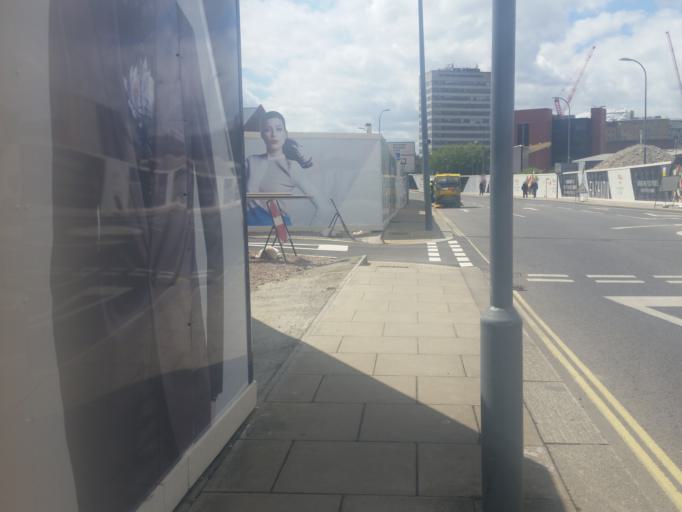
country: GB
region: England
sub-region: Greater London
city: Hammersmith
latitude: 51.5095
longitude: -0.2203
